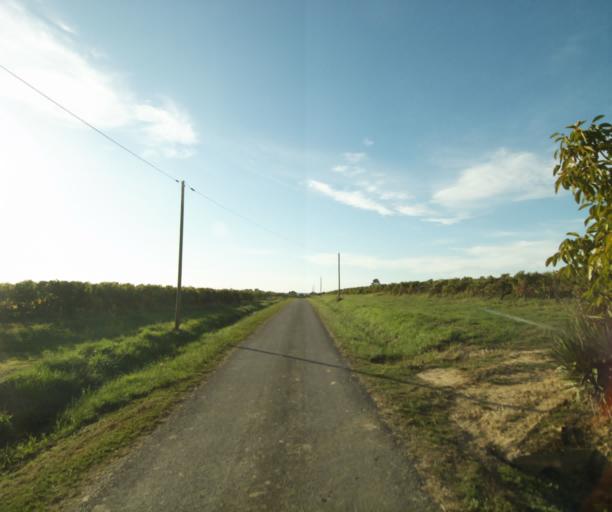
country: FR
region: Midi-Pyrenees
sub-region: Departement du Gers
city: Eauze
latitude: 43.8496
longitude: 0.0187
